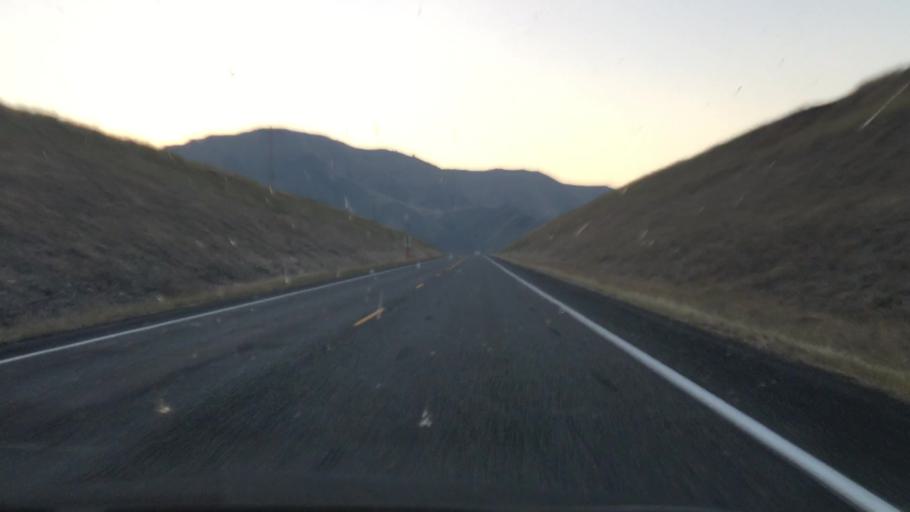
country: US
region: Idaho
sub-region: Idaho County
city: Grangeville
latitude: 45.6696
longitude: -116.3013
